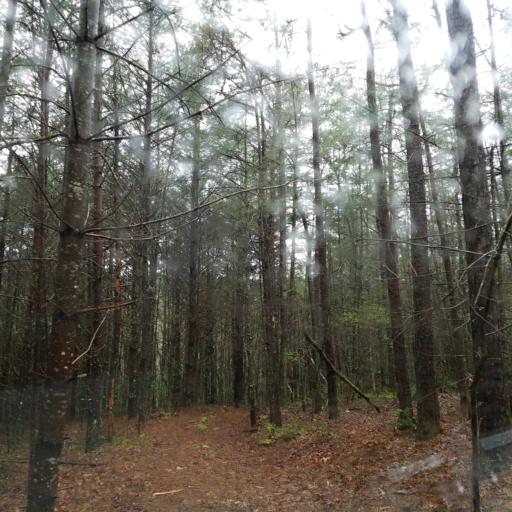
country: US
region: Georgia
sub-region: Fannin County
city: Blue Ridge
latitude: 34.8358
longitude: -84.2371
